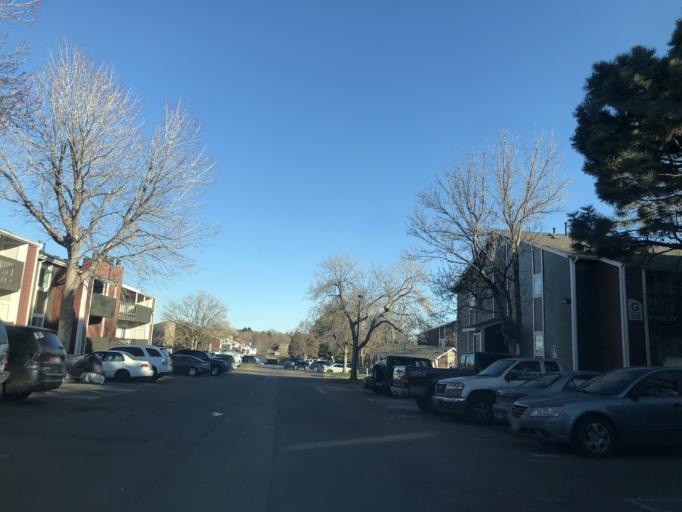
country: US
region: Colorado
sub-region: Adams County
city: Aurora
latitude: 39.7041
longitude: -104.8089
